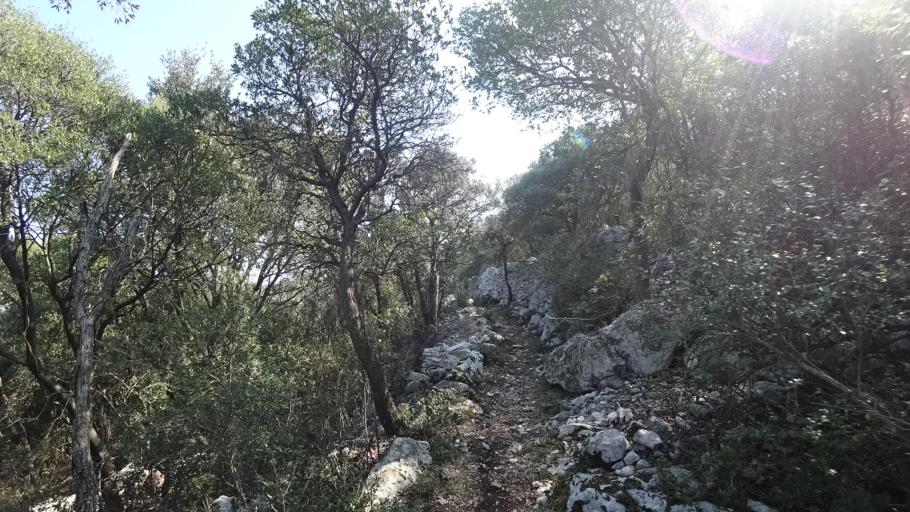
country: HR
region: Primorsko-Goranska
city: Mali Losinj
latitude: 44.4959
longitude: 14.5268
